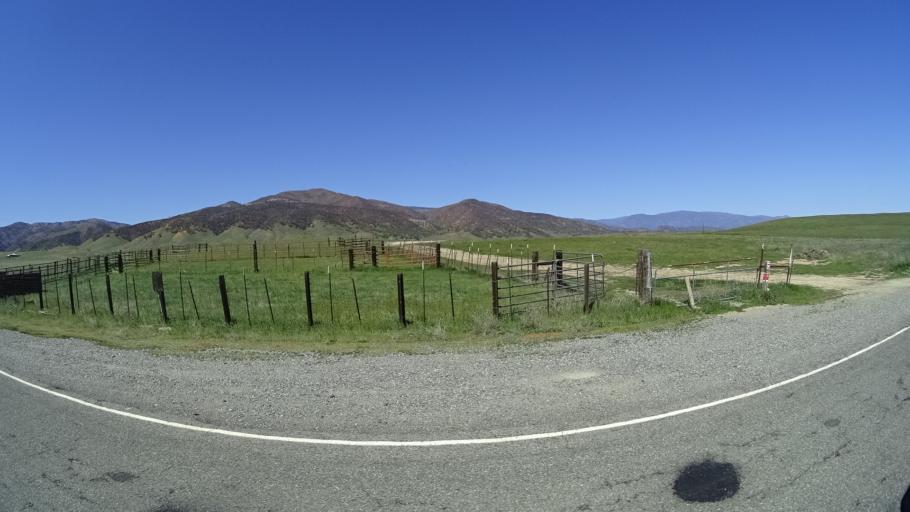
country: US
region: California
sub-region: Tehama County
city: Rancho Tehama Reserve
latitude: 39.7364
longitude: -122.5469
